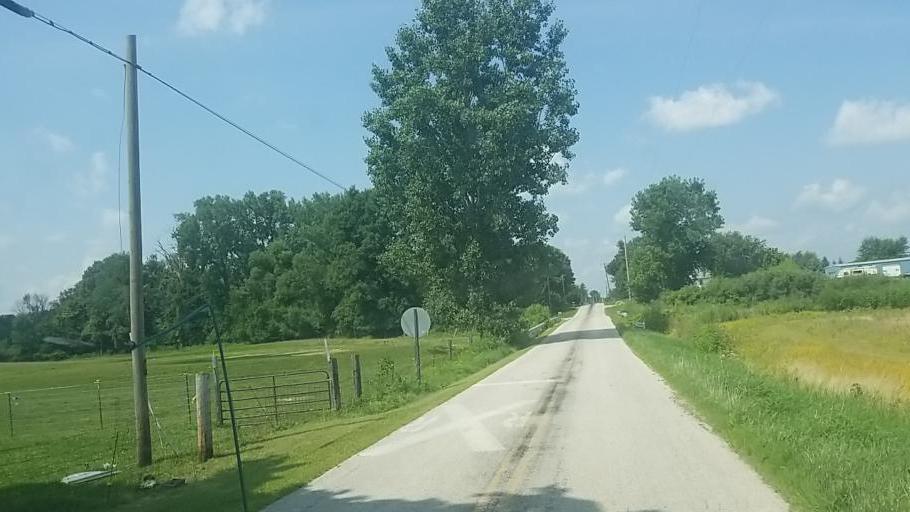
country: US
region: Ohio
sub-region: Crawford County
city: Crestline
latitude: 40.7988
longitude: -82.6735
